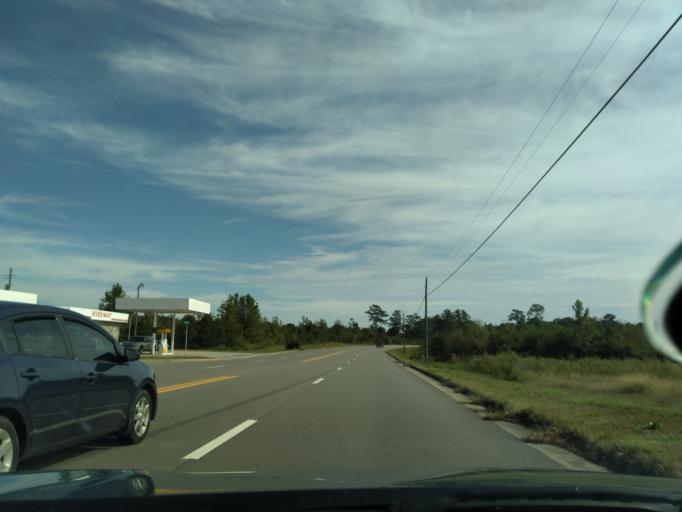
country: US
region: North Carolina
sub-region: Beaufort County
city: River Road
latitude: 35.5288
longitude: -77.0146
